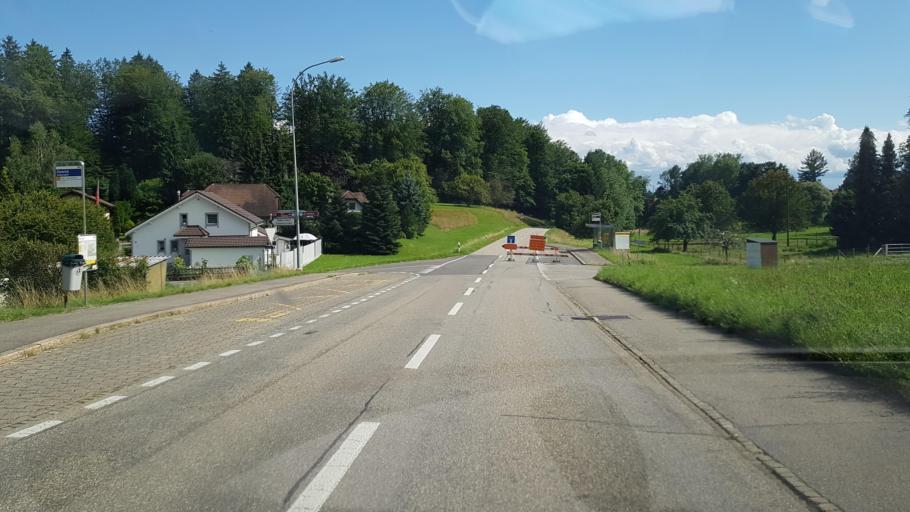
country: CH
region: Solothurn
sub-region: Bezirk Lebern
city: Riedholz
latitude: 47.2417
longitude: 7.5844
